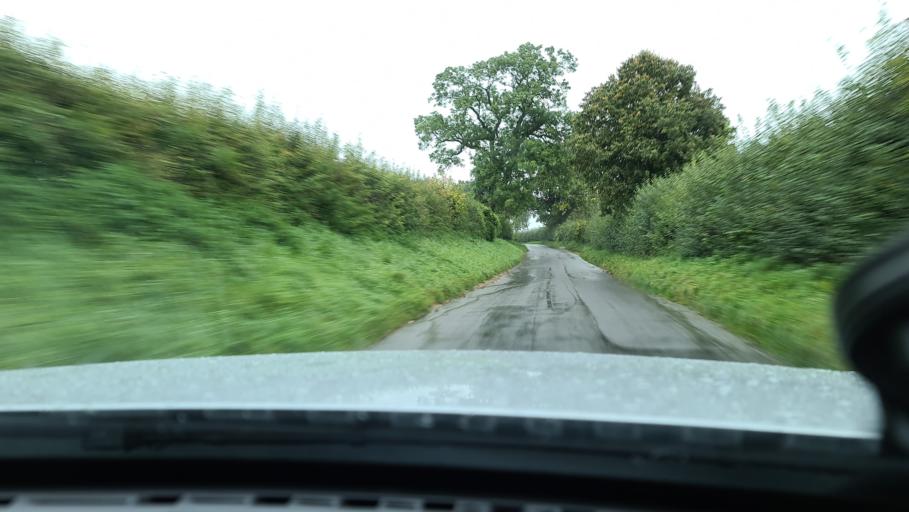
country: GB
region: England
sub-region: Oxfordshire
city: Woodstock
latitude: 51.8932
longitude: -1.3793
